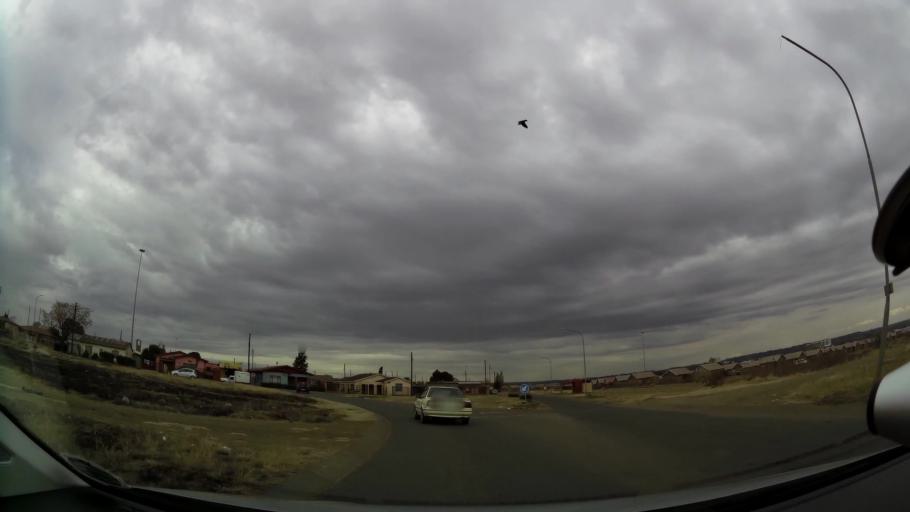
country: ZA
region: Orange Free State
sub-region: Fezile Dabi District Municipality
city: Kroonstad
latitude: -27.6565
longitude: 27.2014
